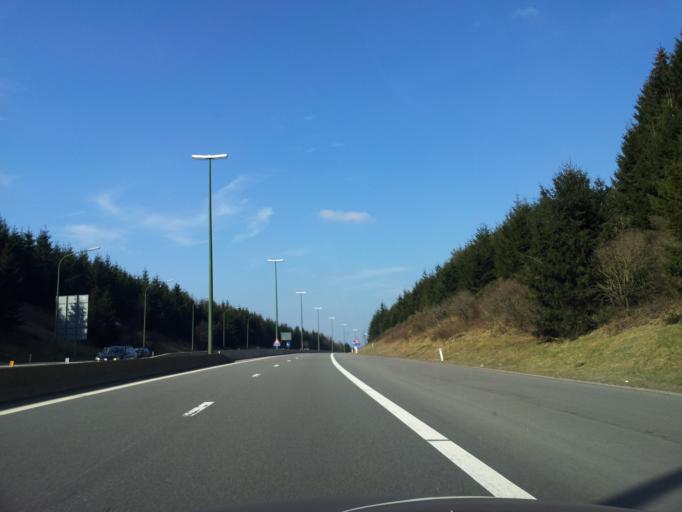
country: BE
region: Wallonia
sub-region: Province de Liege
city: Jalhay
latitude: 50.4797
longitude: 5.9601
